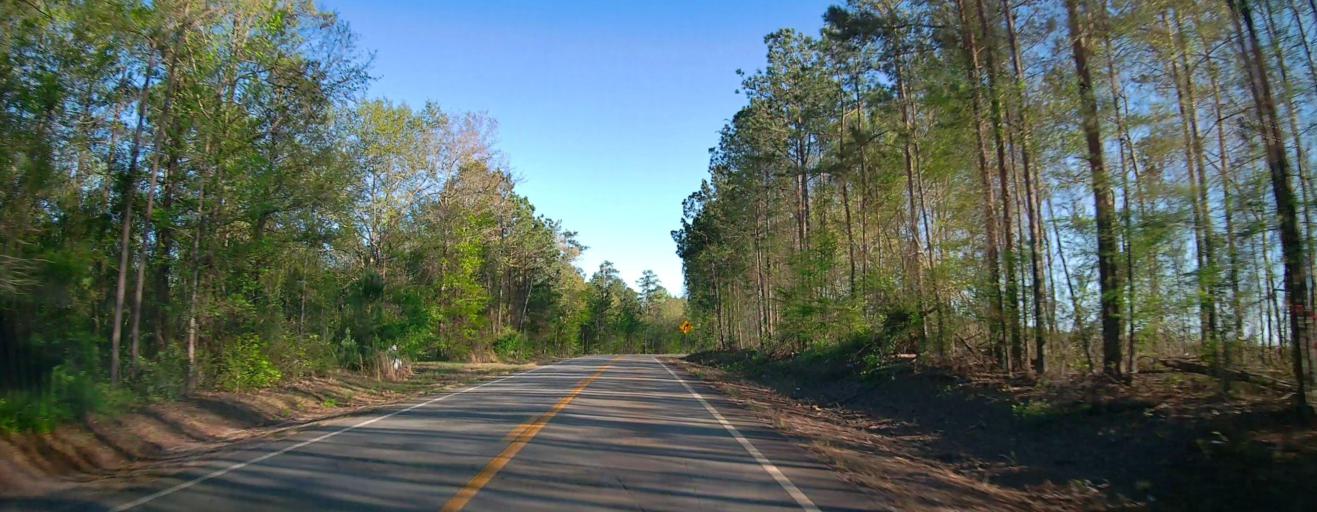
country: US
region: Georgia
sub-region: Wilkinson County
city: Irwinton
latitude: 32.8503
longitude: -83.0632
